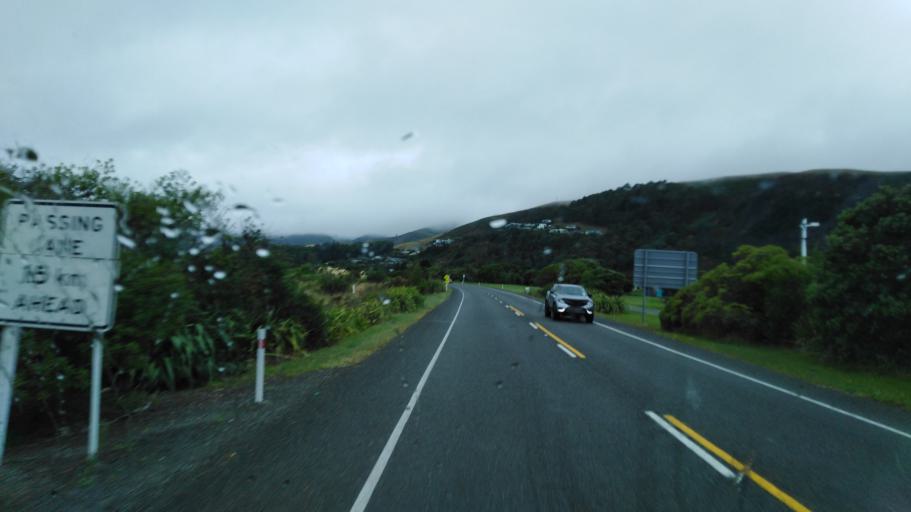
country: NZ
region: Nelson
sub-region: Nelson City
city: Nelson
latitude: -41.2639
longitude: 173.2882
